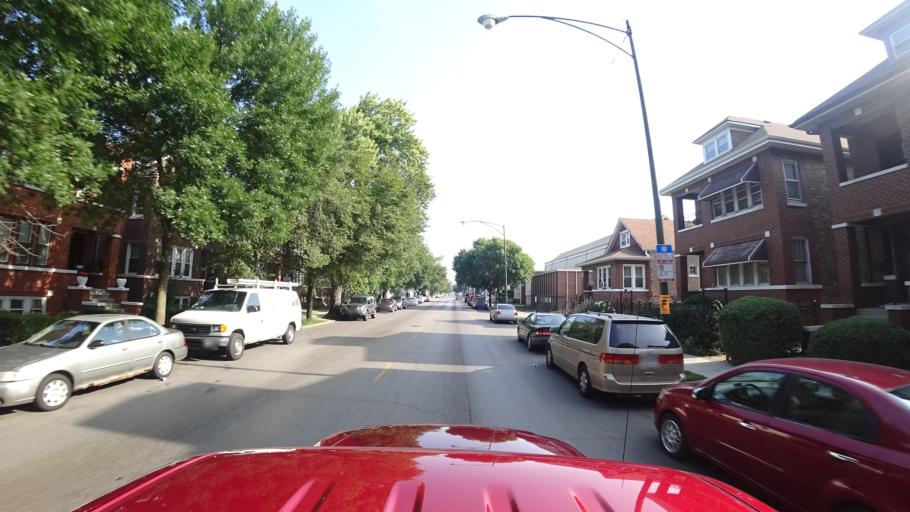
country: US
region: Illinois
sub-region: Cook County
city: Chicago
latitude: 41.8125
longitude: -87.6943
